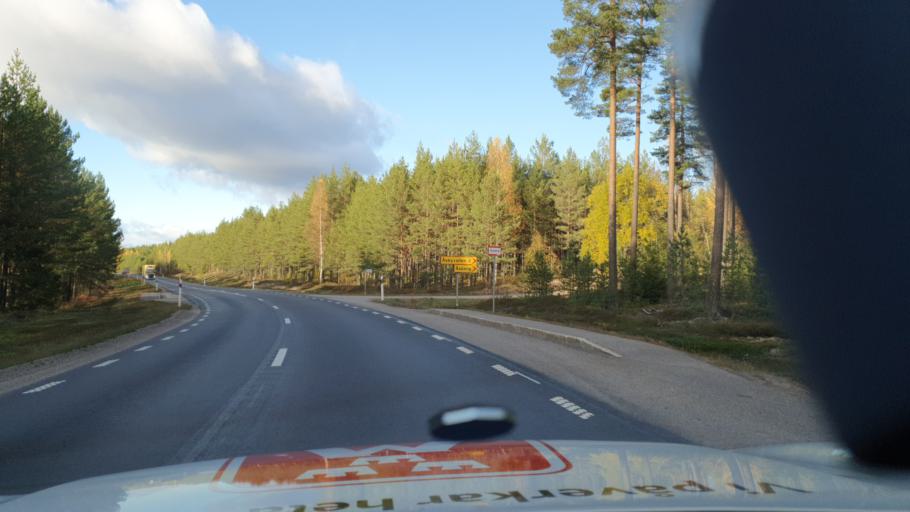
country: SE
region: Gaevleborg
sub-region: Gavle Kommun
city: Hedesunda
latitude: 60.4507
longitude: 16.9597
